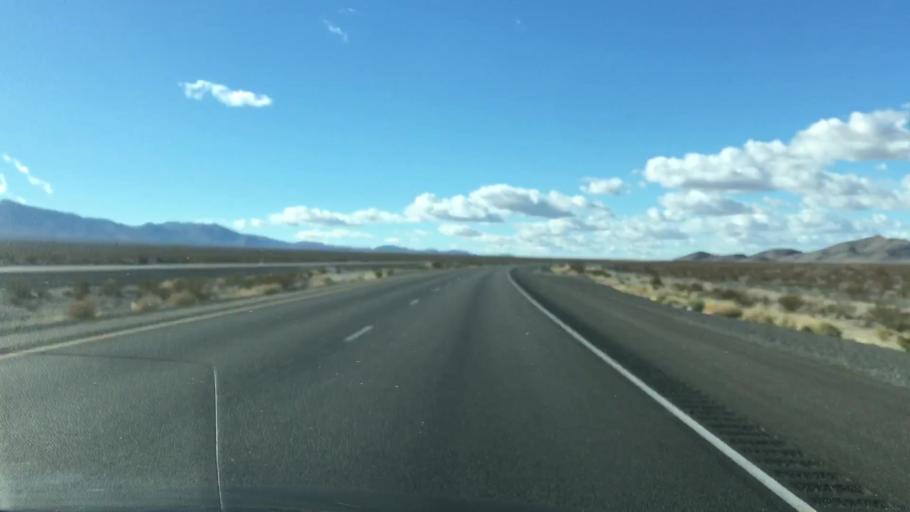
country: US
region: Nevada
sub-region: Nye County
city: Pahrump
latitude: 36.5681
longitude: -115.8110
